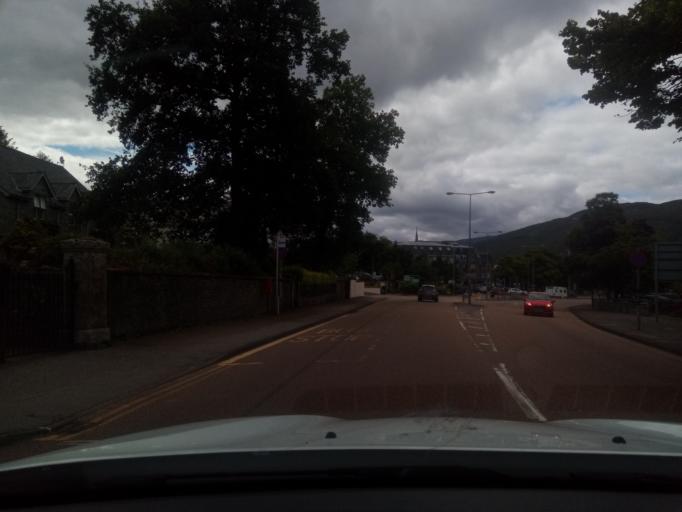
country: GB
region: Scotland
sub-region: Highland
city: Fort William
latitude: 56.8199
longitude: -5.1037
